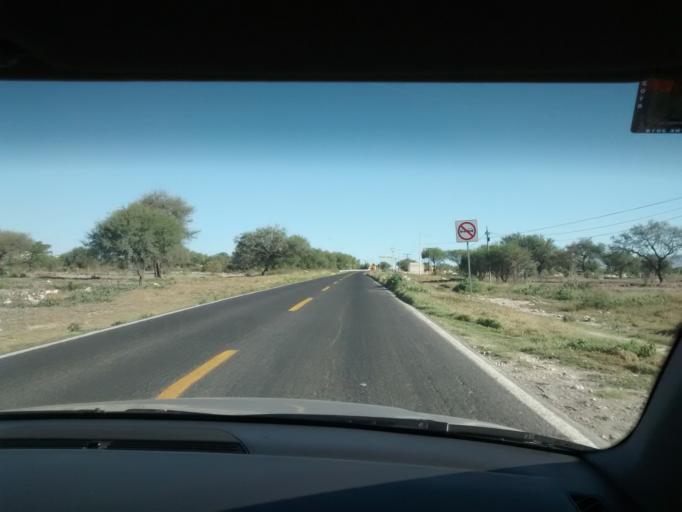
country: MX
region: Puebla
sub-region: Tepanco de Lopez
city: San Andres Cacaloapan
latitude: 18.5721
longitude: -97.5754
